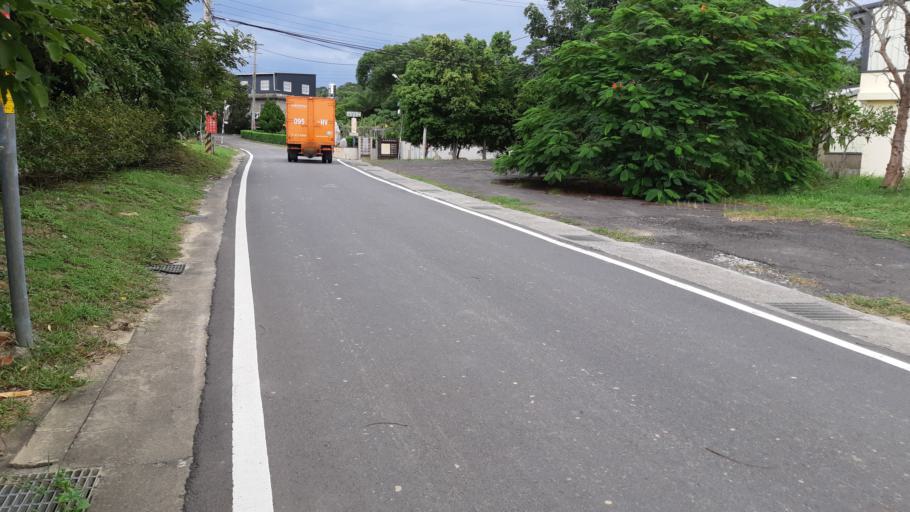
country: TW
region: Taiwan
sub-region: Miaoli
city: Miaoli
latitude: 24.6571
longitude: 120.8907
